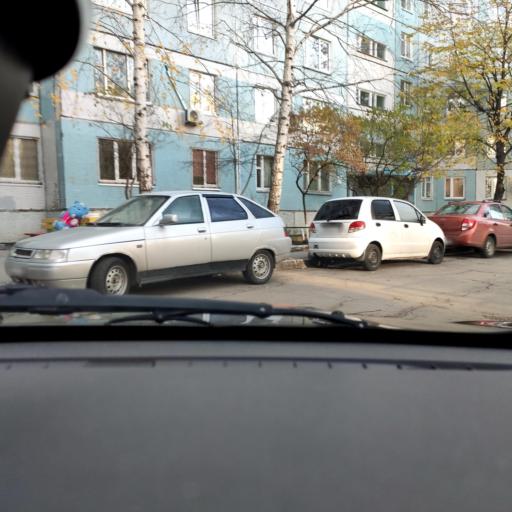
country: RU
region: Samara
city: Tol'yatti
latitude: 53.5469
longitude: 49.3412
